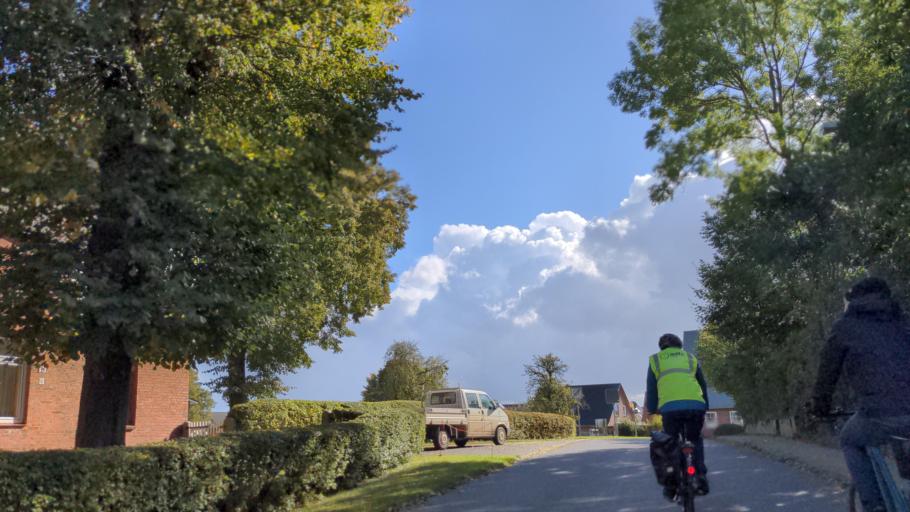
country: DE
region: Schleswig-Holstein
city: Reinfeld
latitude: 53.8277
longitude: 10.5083
